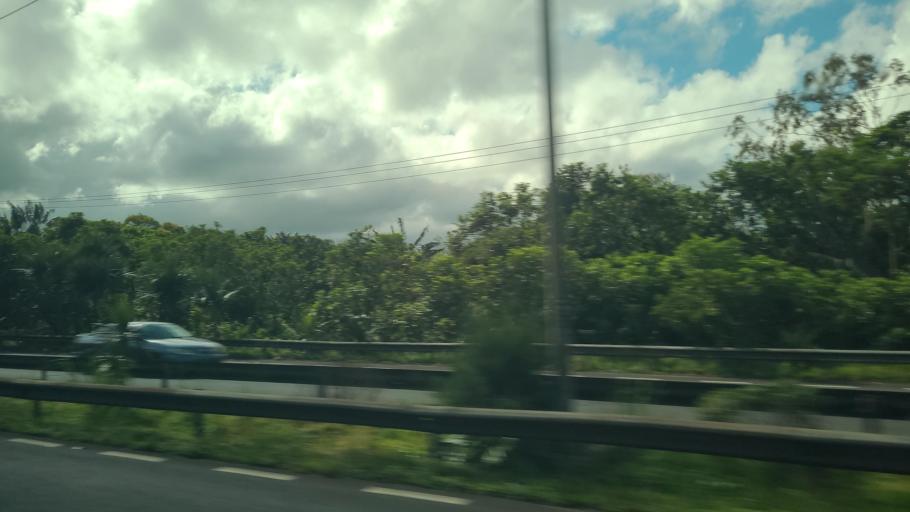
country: MU
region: Plaines Wilhems
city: Midlands
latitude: -20.3308
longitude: 57.5531
